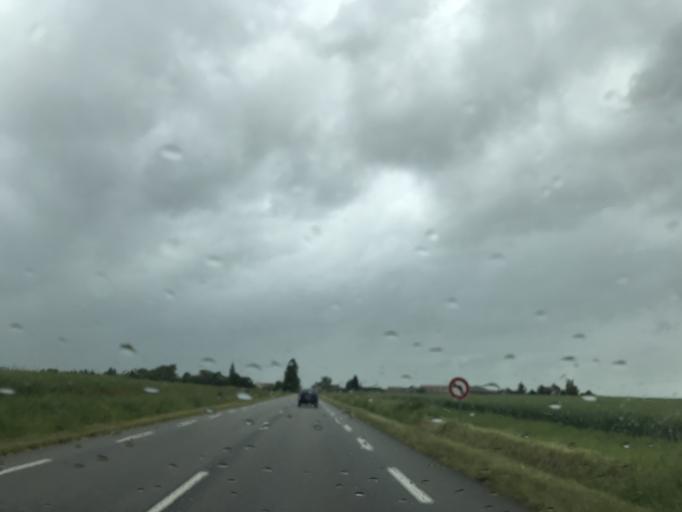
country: FR
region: Haute-Normandie
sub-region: Departement de l'Eure
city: La Couture-Boussey
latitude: 48.9096
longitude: 1.3539
